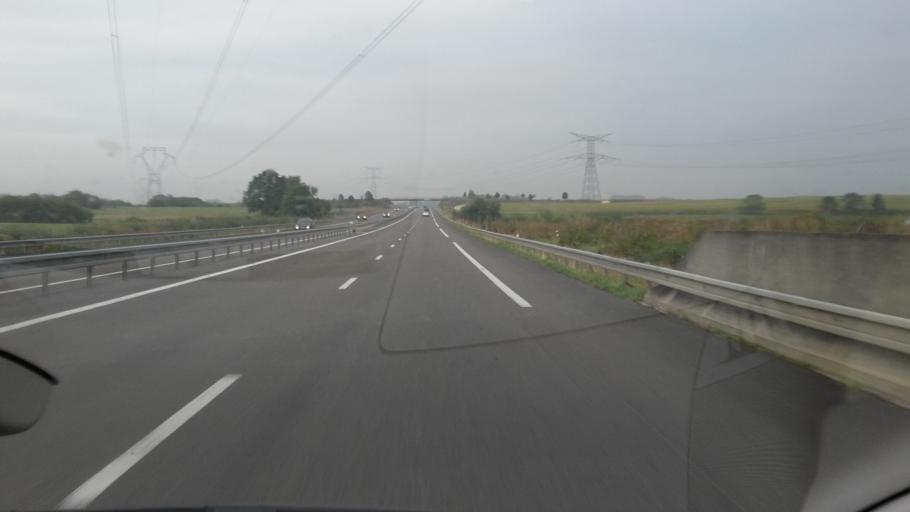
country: FR
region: Champagne-Ardenne
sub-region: Departement des Ardennes
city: Rethel
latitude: 49.5710
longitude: 4.4745
